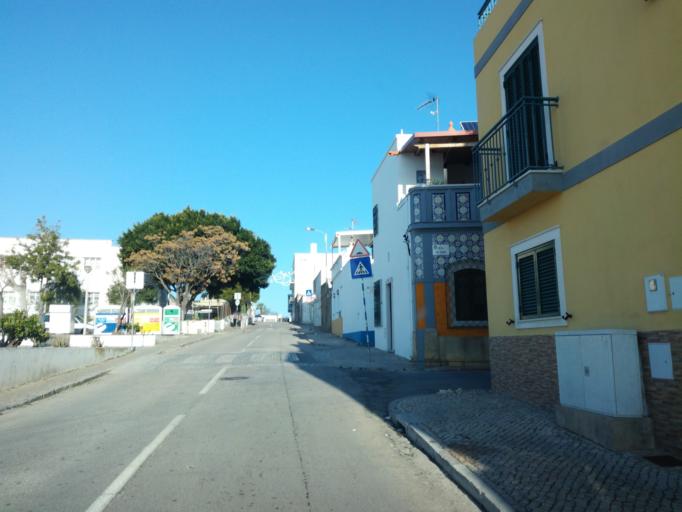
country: PT
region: Faro
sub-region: Olhao
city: Laranjeiro
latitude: 37.0536
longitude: -7.7482
